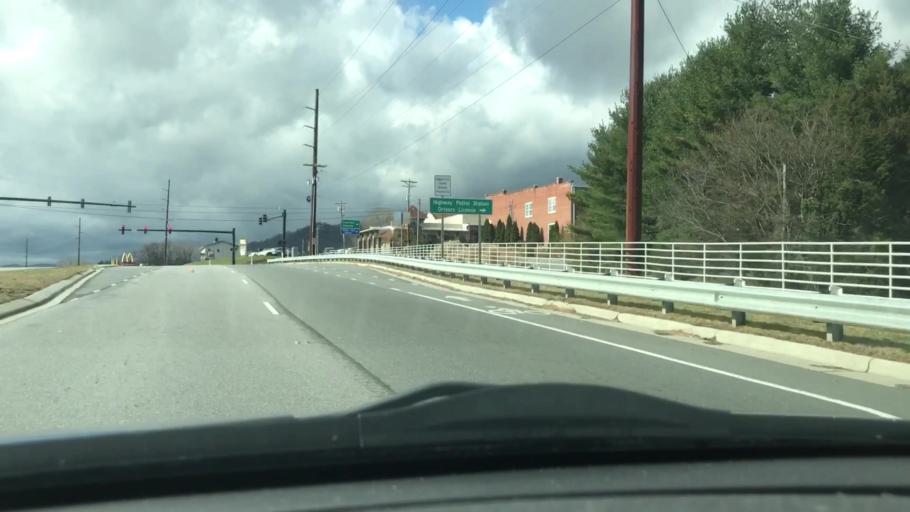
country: US
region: North Carolina
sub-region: Yancey County
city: Burnsville
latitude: 35.9158
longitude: -82.2984
